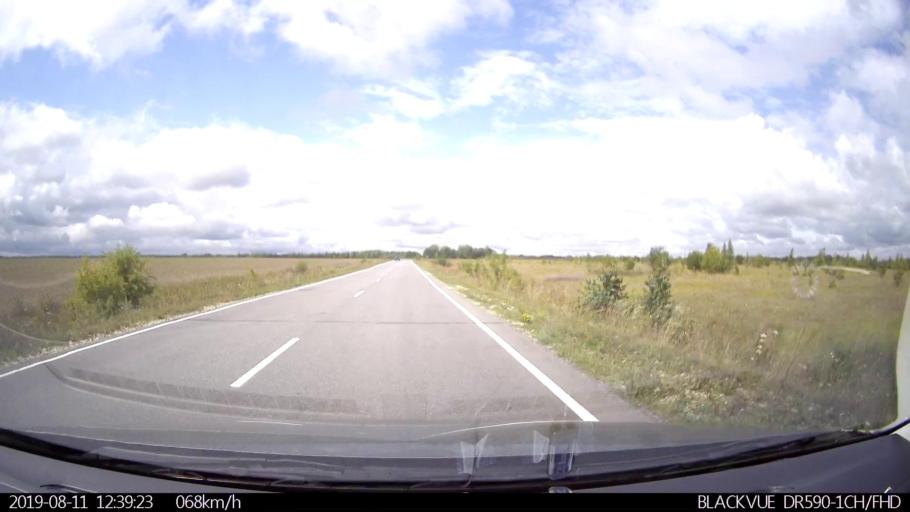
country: RU
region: Ulyanovsk
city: Ignatovka
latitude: 53.8330
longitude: 47.7964
